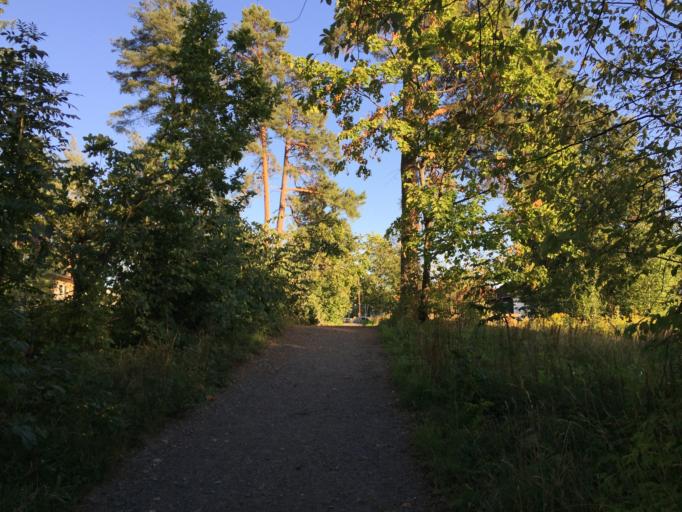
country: NO
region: Akershus
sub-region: Baerum
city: Lysaker
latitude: 59.9011
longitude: 10.6109
